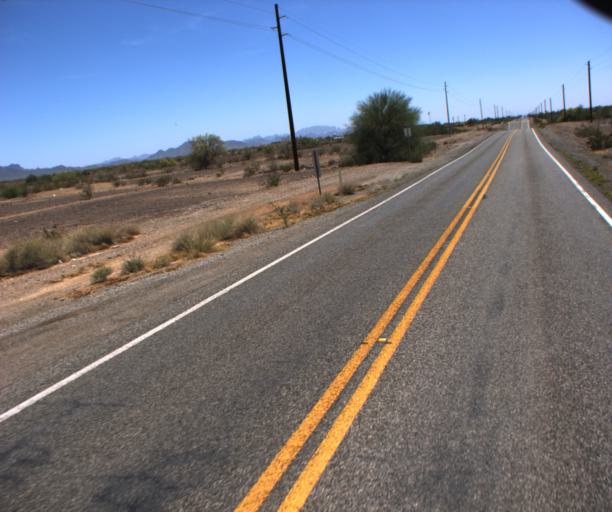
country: US
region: Arizona
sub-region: La Paz County
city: Quartzsite
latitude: 33.6953
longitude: -114.2171
